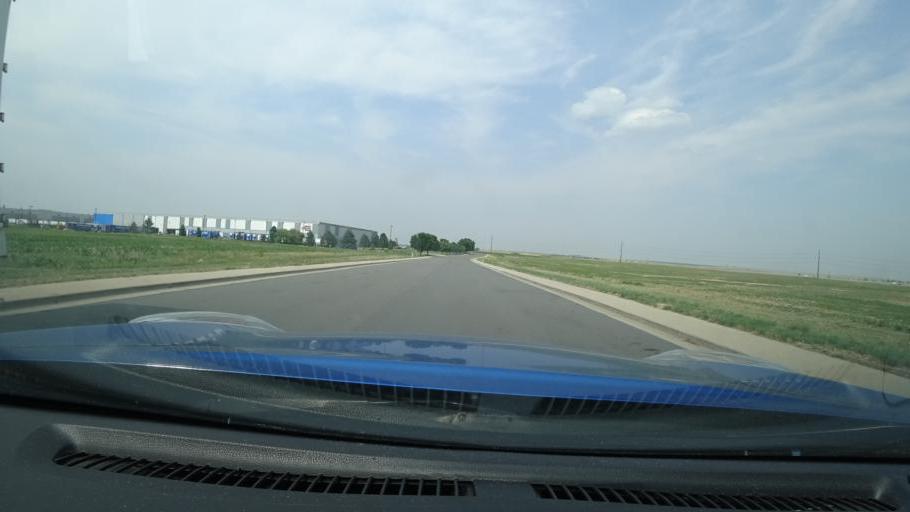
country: US
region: Colorado
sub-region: Adams County
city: Aurora
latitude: 39.7593
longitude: -104.7405
